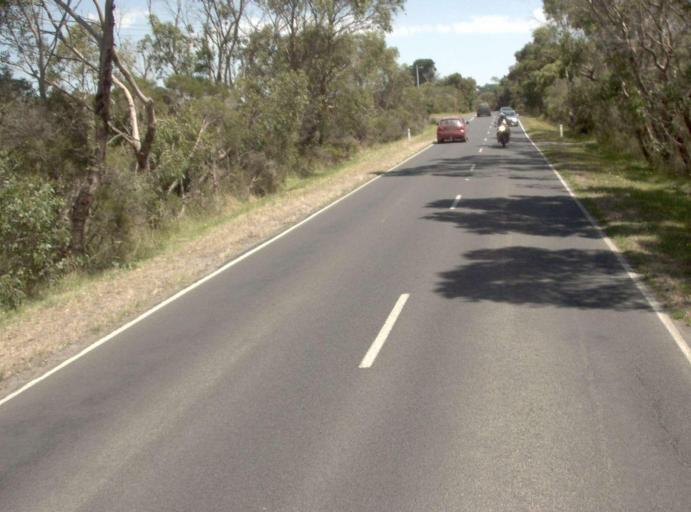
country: AU
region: Victoria
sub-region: Bass Coast
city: North Wonthaggi
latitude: -38.6317
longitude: 145.8391
